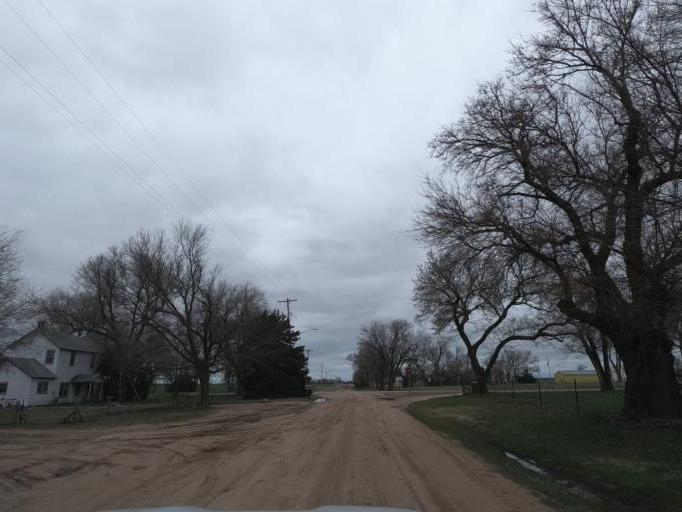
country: US
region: Kansas
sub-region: Rice County
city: Sterling
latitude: 37.9708
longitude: -98.3072
